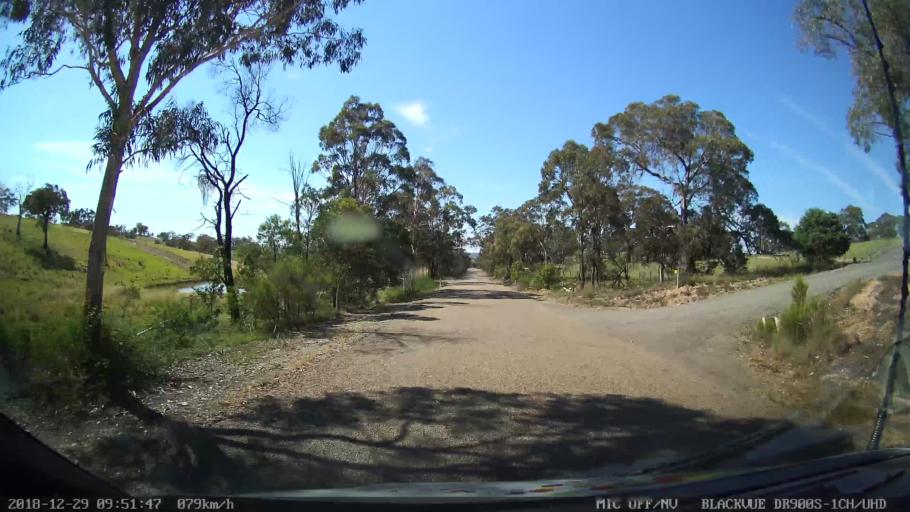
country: AU
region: New South Wales
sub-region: Goulburn Mulwaree
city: Goulburn
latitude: -34.7360
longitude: 149.4618
